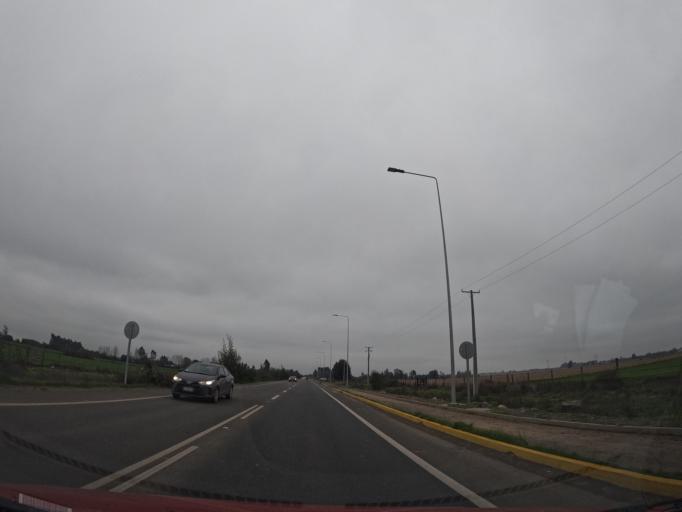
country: CL
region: Maule
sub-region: Provincia de Talca
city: San Clemente
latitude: -35.5175
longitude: -71.4959
